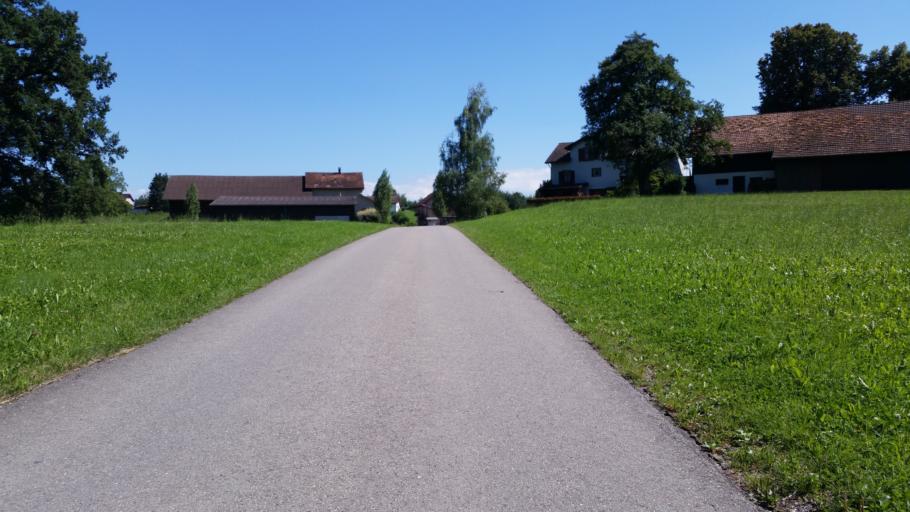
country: CH
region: Saint Gallen
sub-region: Wahlkreis Wil
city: Uzwil
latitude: 47.4409
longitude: 9.1610
